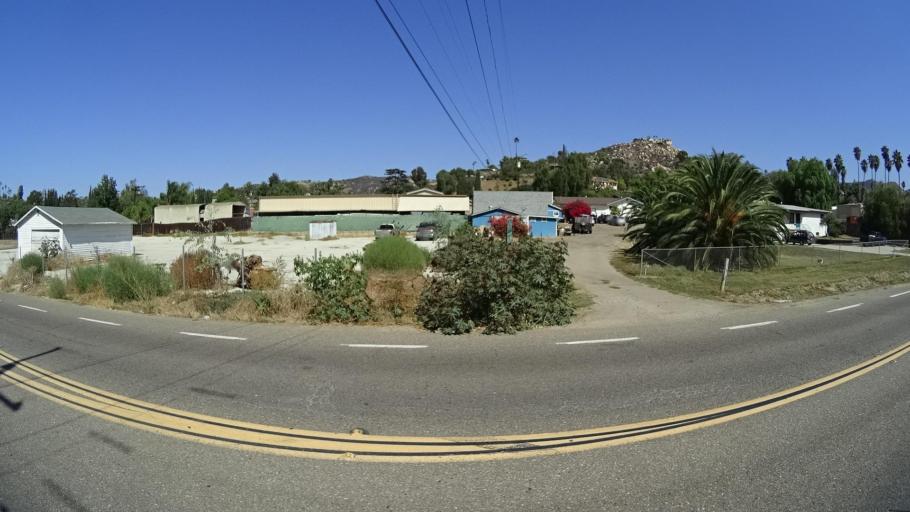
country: US
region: California
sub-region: San Diego County
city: Granite Hills
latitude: 32.8066
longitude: -116.9102
